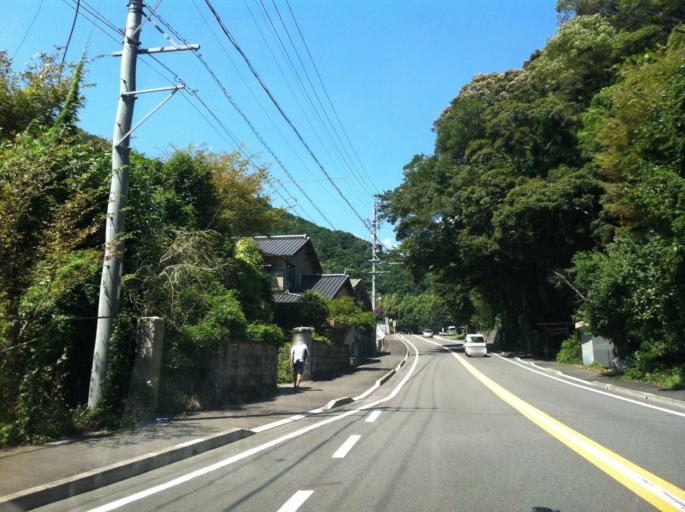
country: JP
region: Shizuoka
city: Shizuoka-shi
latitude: 35.0141
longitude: 138.2708
